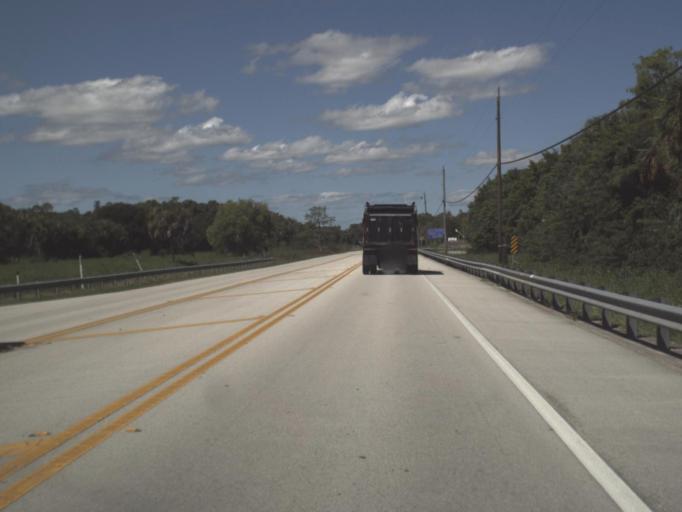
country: US
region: Florida
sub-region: Collier County
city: Lely Resort
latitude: 26.0177
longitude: -81.6277
